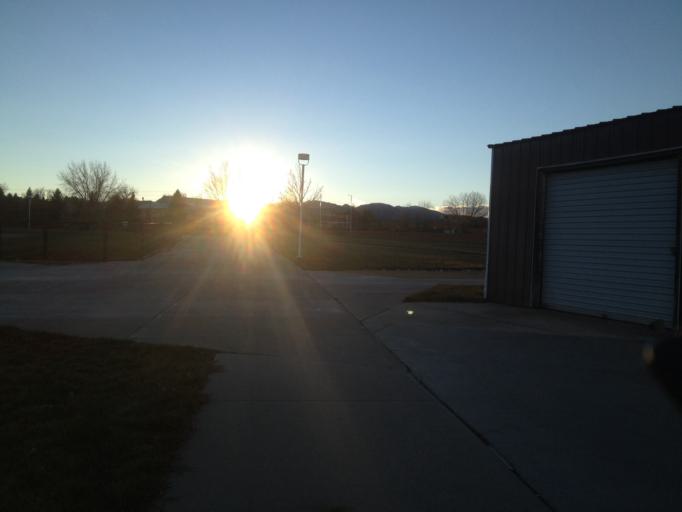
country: US
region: Colorado
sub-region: Boulder County
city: Superior
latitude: 39.9532
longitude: -105.1442
